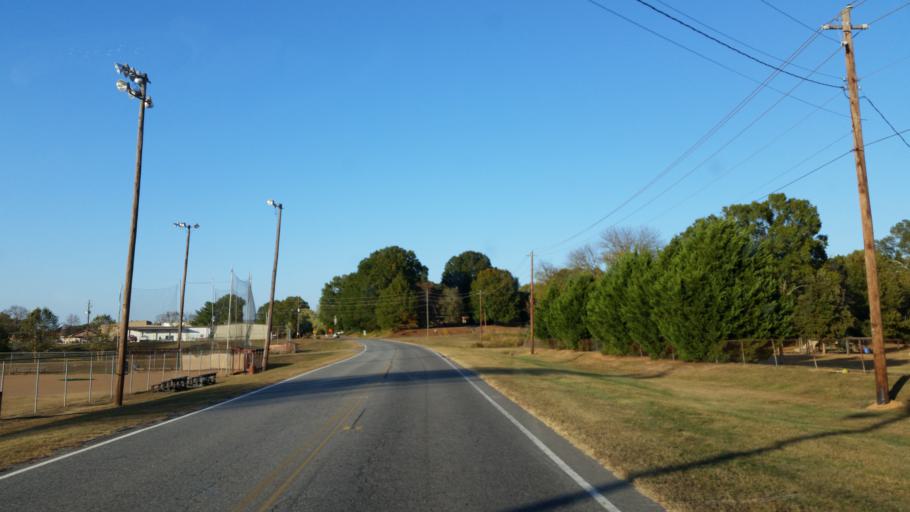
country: US
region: Georgia
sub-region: Bartow County
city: Adairsville
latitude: 34.3715
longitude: -84.9410
